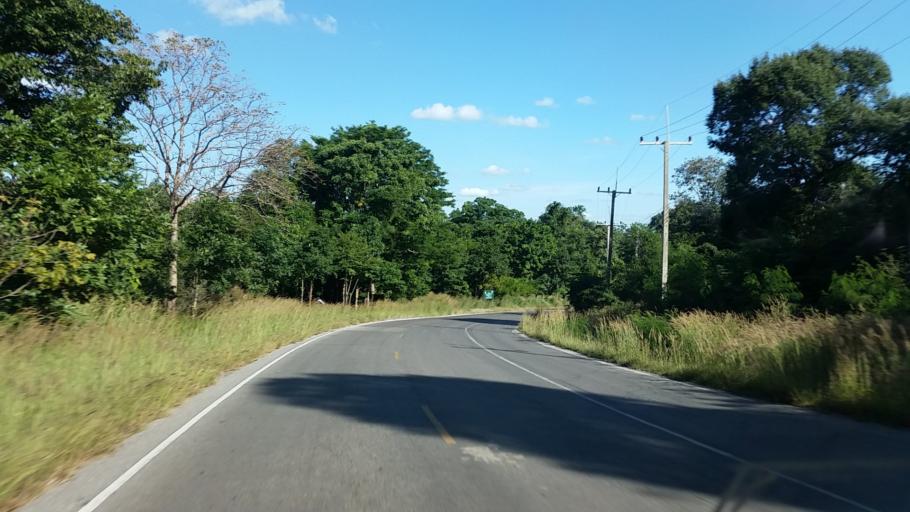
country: TH
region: Chaiyaphum
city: Thep Sathit
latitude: 15.5361
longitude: 101.4204
